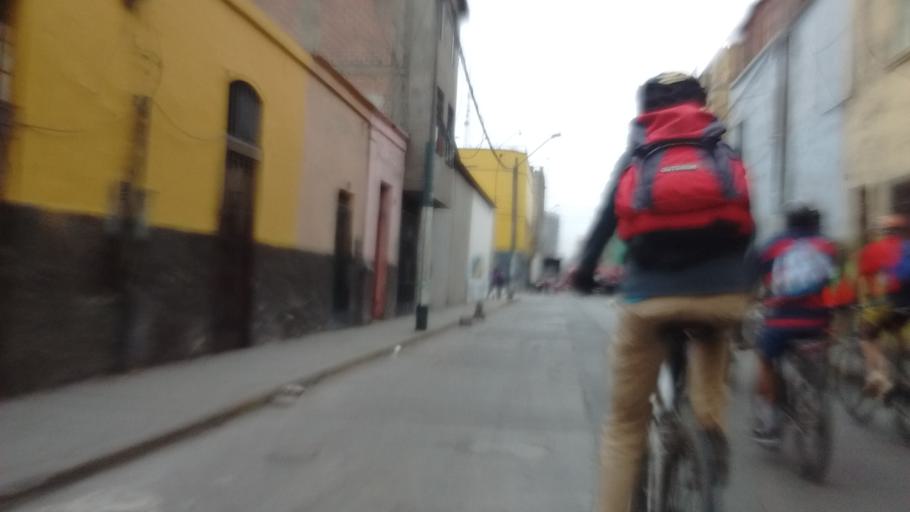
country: PE
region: Lima
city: Lima
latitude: -12.0650
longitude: -77.0283
